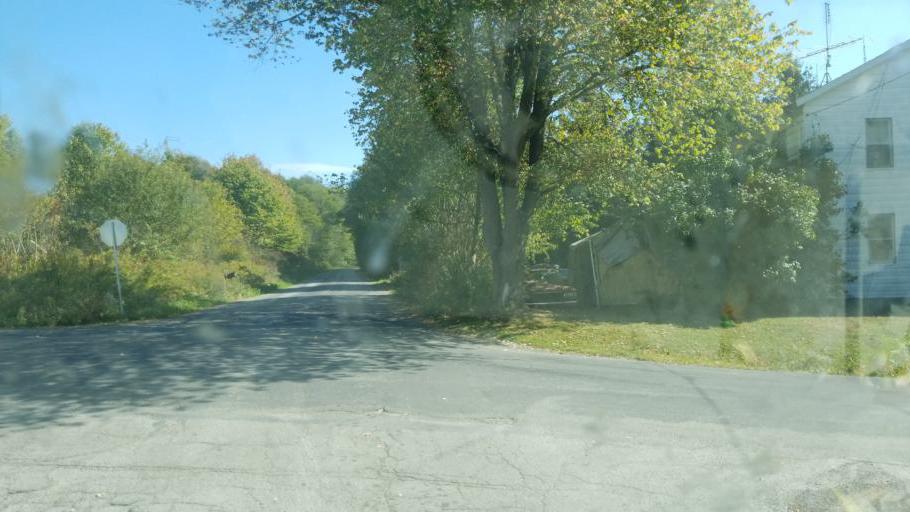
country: US
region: Pennsylvania
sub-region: Mercer County
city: Greenville
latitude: 41.3817
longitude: -80.4207
